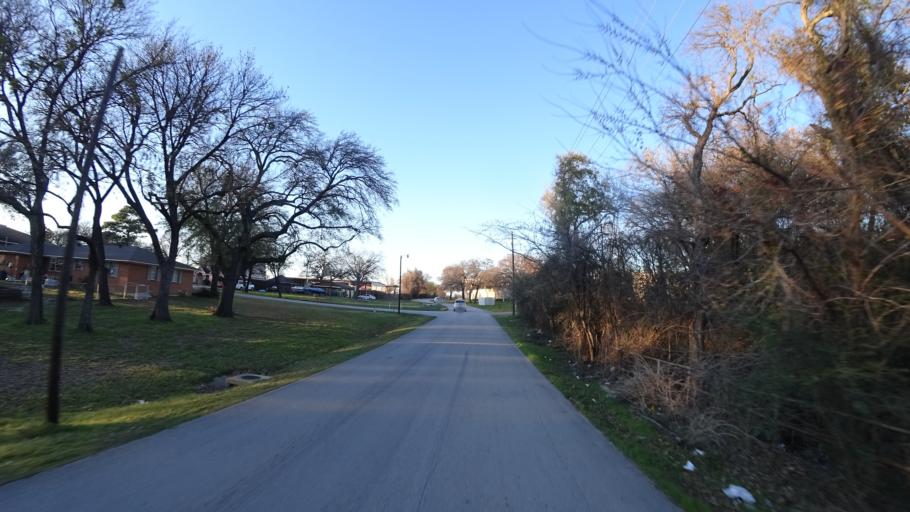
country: US
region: Texas
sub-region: Denton County
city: Lewisville
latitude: 33.0284
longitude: -96.9872
